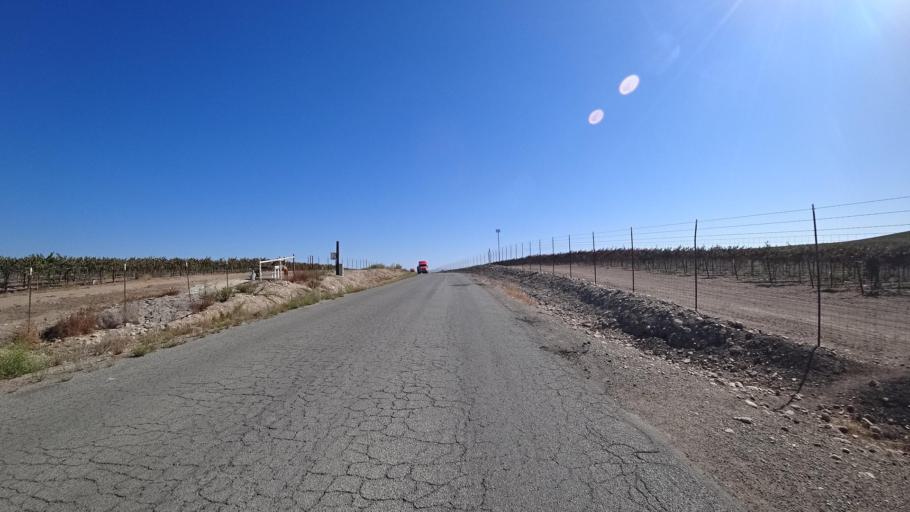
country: US
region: California
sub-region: Monterey County
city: King City
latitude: 36.1692
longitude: -121.1280
